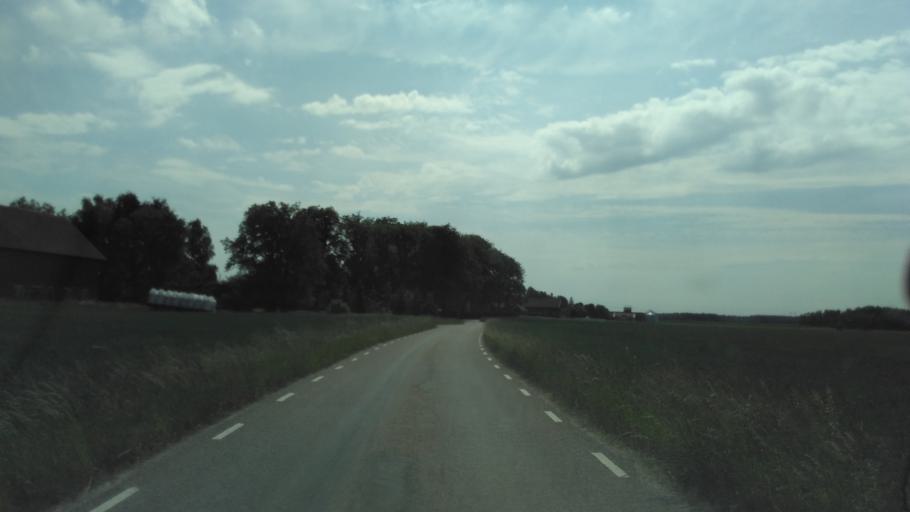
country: SE
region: Vaestra Goetaland
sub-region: Grastorps Kommun
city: Graestorp
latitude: 58.3921
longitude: 12.7924
